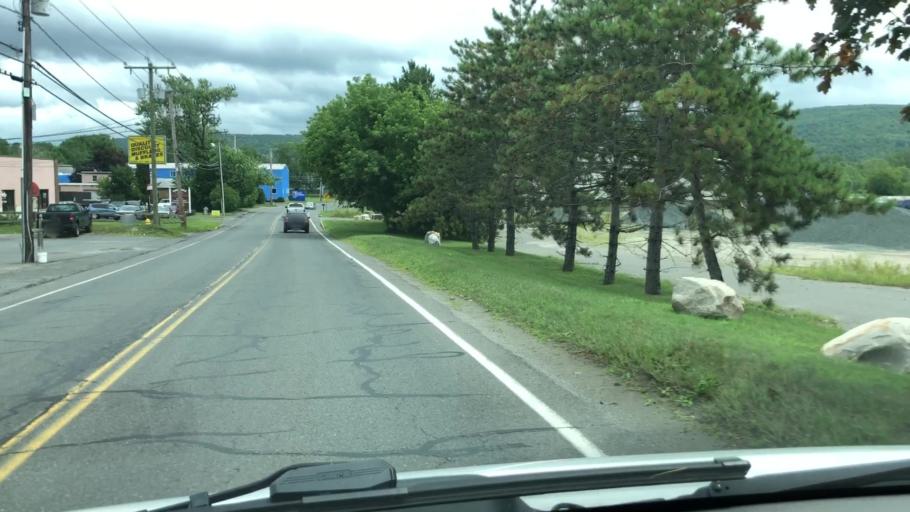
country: US
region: Massachusetts
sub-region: Berkshire County
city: Pittsfield
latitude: 42.4546
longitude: -73.2107
